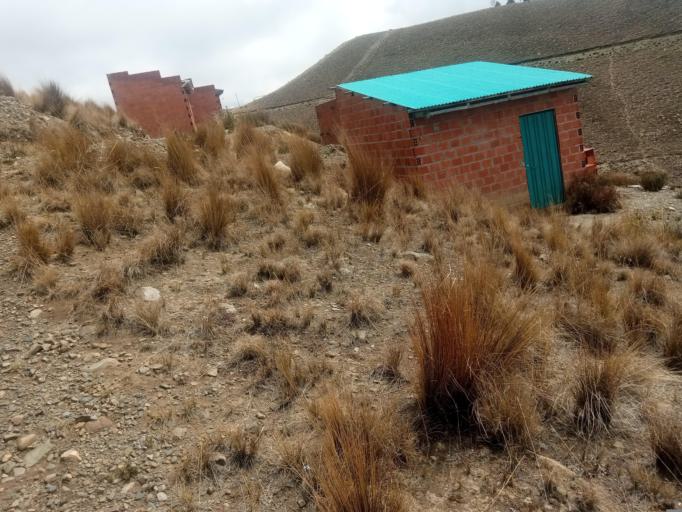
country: BO
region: La Paz
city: La Paz
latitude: -16.4619
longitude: -68.1370
